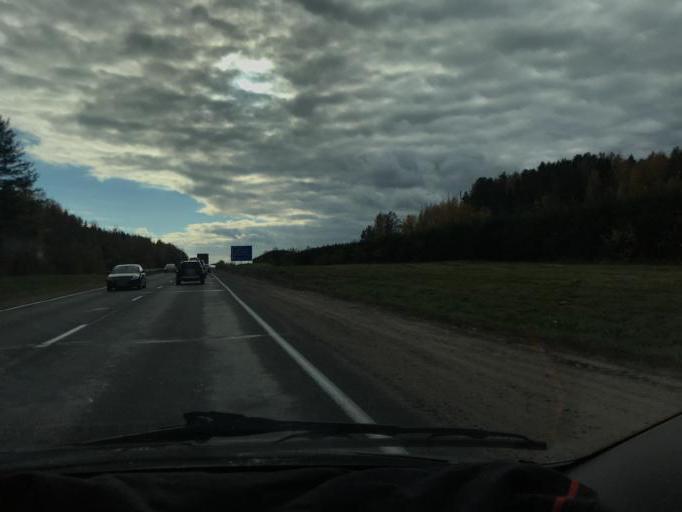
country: BY
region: Minsk
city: Lahoysk
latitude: 54.2155
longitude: 27.8295
